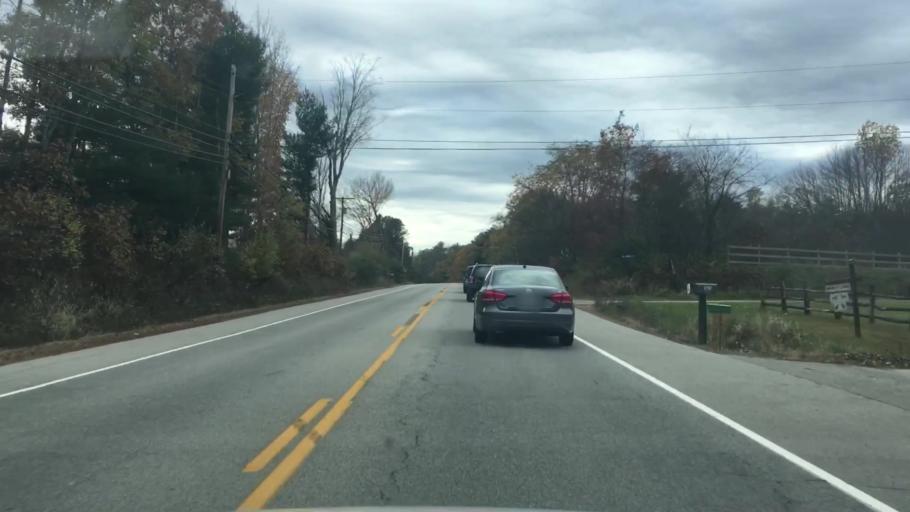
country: US
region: Maine
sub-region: York County
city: West Kennebunk
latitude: 43.4795
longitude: -70.6243
